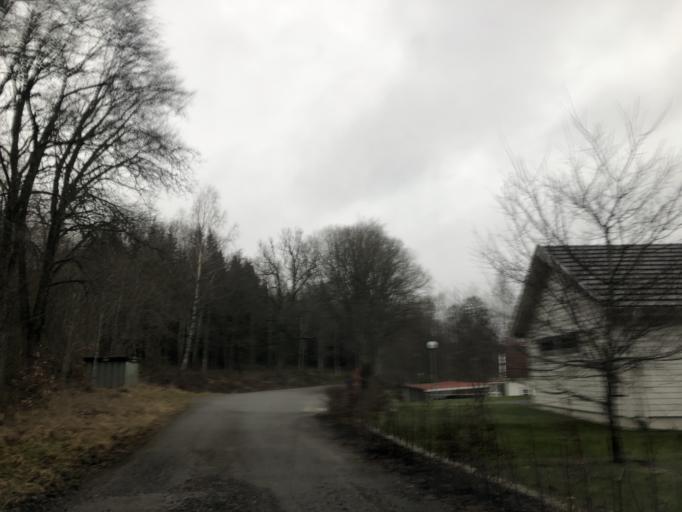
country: SE
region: Vaestra Goetaland
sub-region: Ulricehamns Kommun
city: Ulricehamn
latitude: 57.7911
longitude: 13.3914
